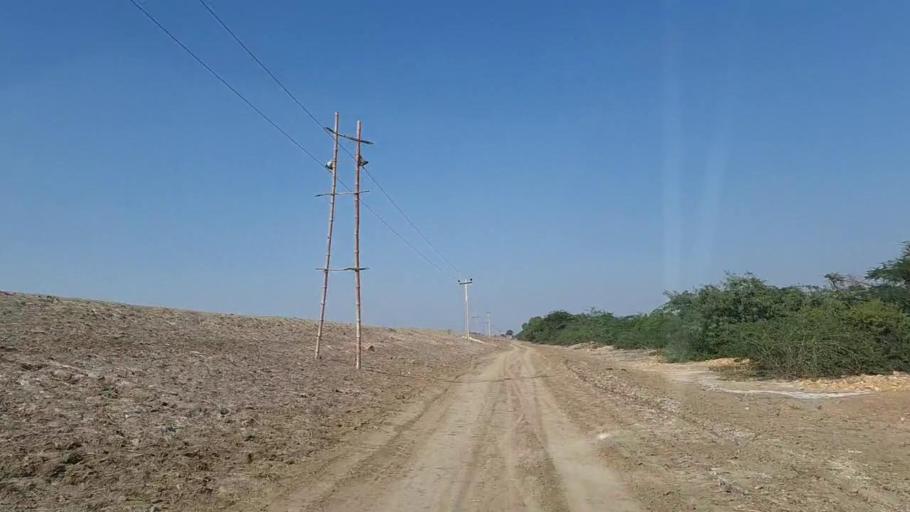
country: PK
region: Sindh
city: Chuhar Jamali
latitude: 24.5425
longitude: 68.0157
